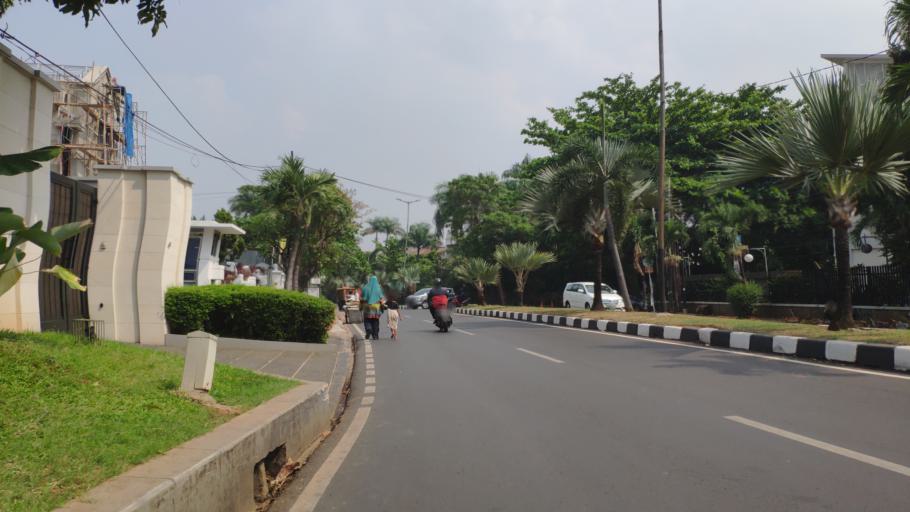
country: ID
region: Banten
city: South Tangerang
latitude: -6.2762
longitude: 106.7767
